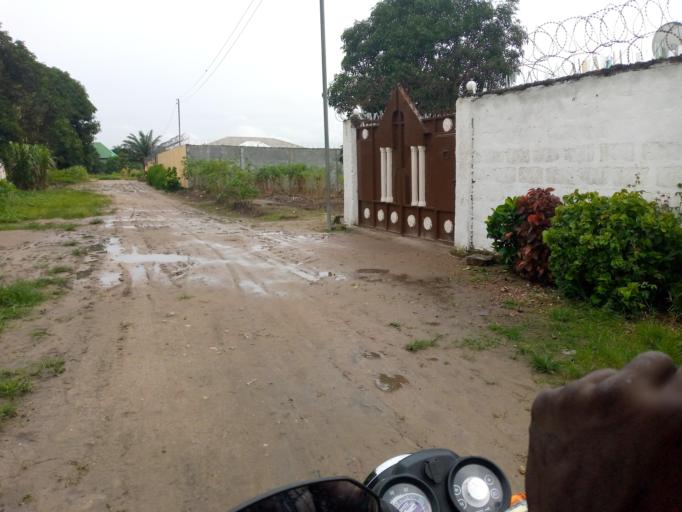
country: SL
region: Eastern Province
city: Kenema
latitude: 7.8456
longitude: -11.2095
